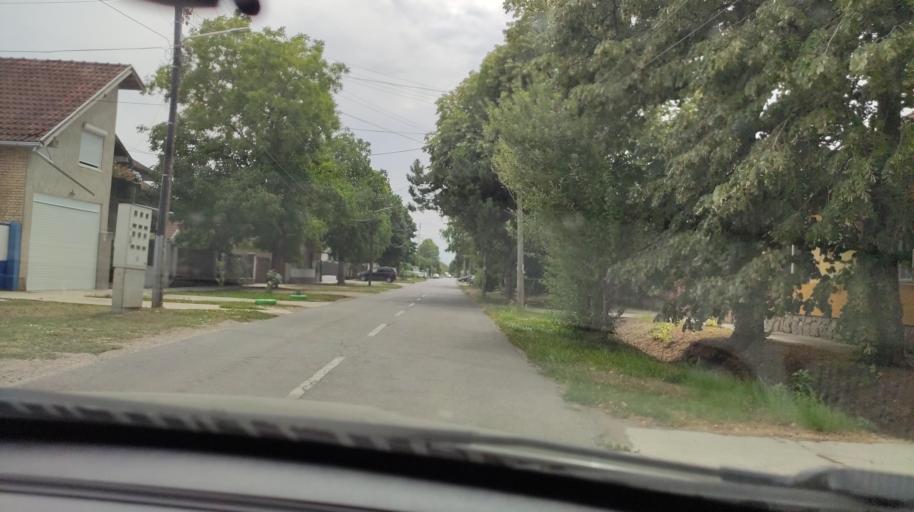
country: RS
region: Autonomna Pokrajina Vojvodina
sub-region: Juznobacki Okrug
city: Temerin
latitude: 45.4125
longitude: 19.8841
